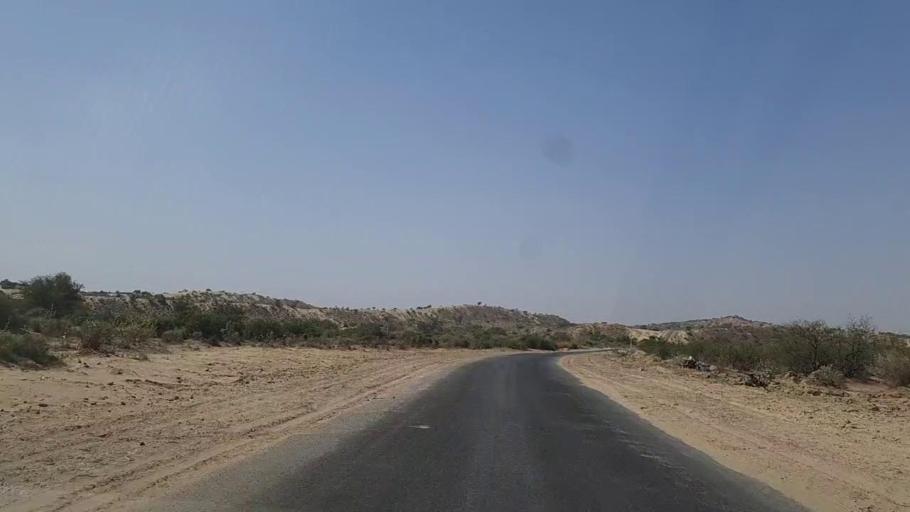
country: PK
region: Sindh
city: Diplo
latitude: 24.5773
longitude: 69.4911
